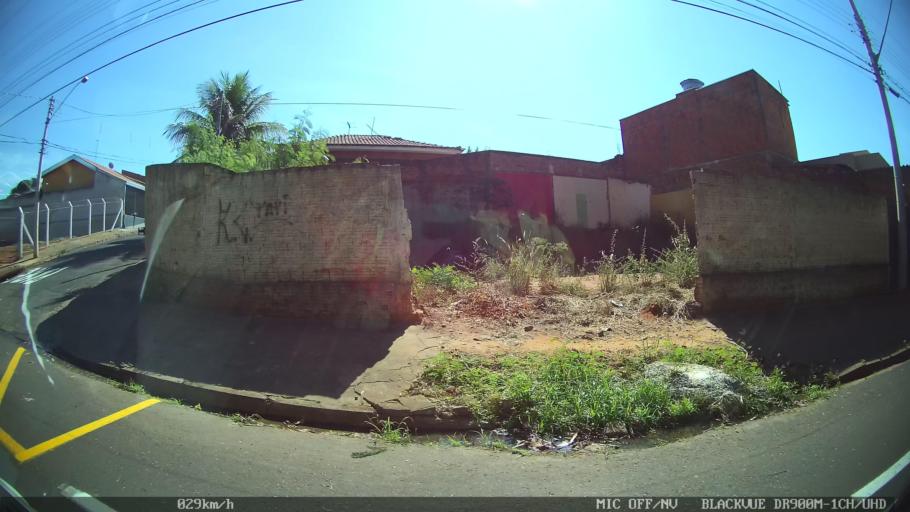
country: BR
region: Sao Paulo
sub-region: Sao Jose Do Rio Preto
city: Sao Jose do Rio Preto
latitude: -20.7729
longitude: -49.4071
